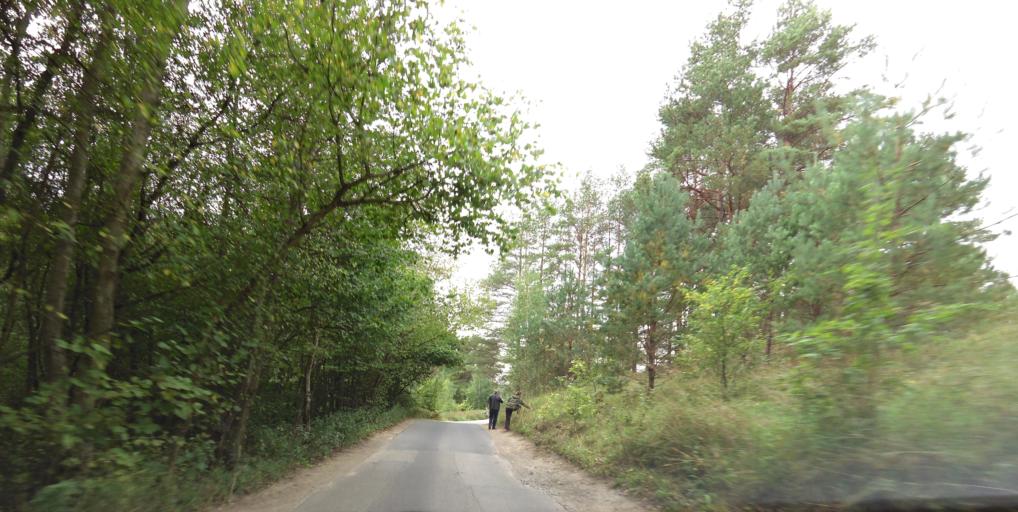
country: LT
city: Grigiskes
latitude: 54.7583
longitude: 25.0363
